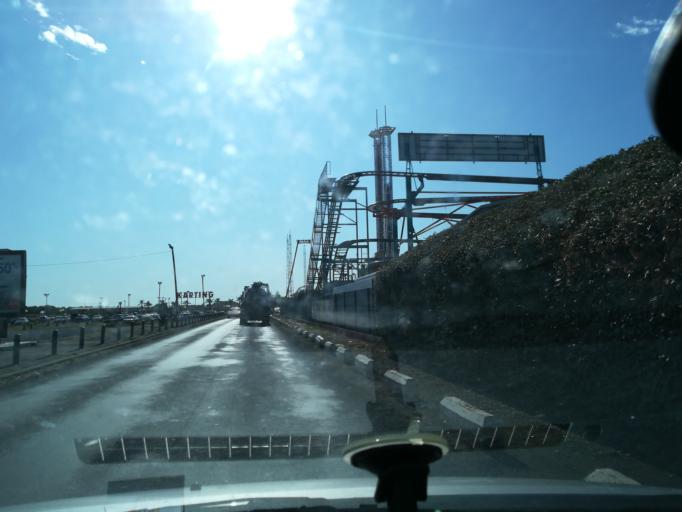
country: FR
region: Languedoc-Roussillon
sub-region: Departement de l'Herault
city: Vias
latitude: 43.3011
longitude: 3.4146
